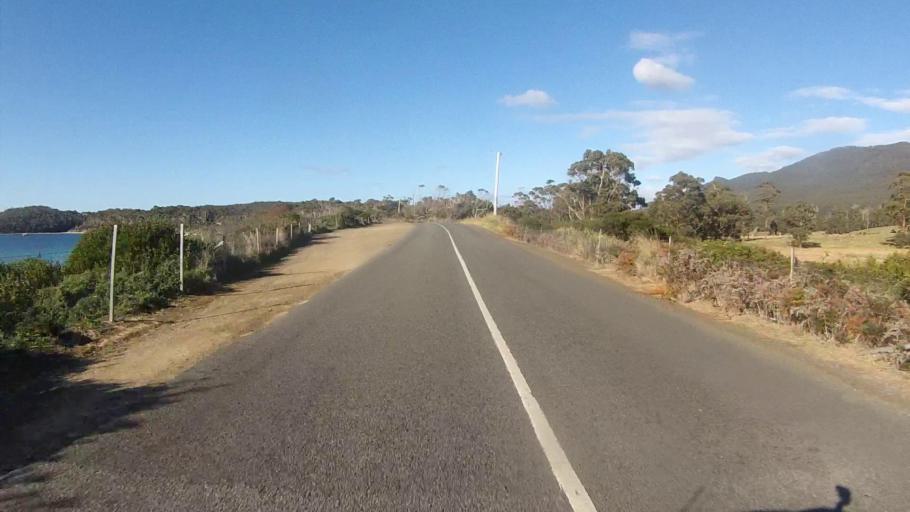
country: AU
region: Tasmania
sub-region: Clarence
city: Sandford
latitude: -43.0351
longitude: 147.9349
